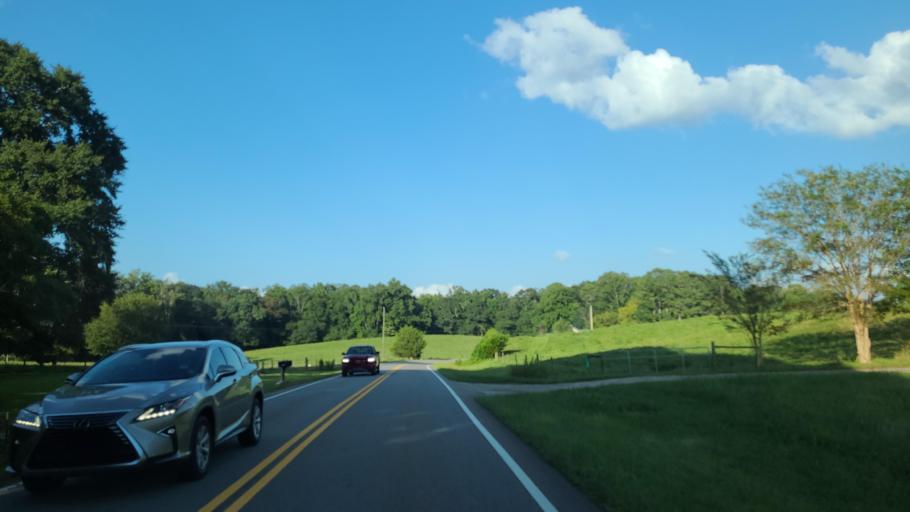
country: US
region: Georgia
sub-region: Cherokee County
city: Holly Springs
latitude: 34.1815
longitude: -84.4102
